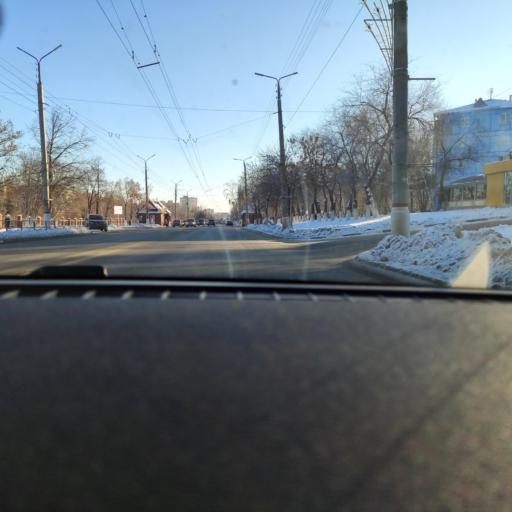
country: RU
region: Samara
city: Novokuybyshevsk
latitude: 53.0996
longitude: 49.9617
